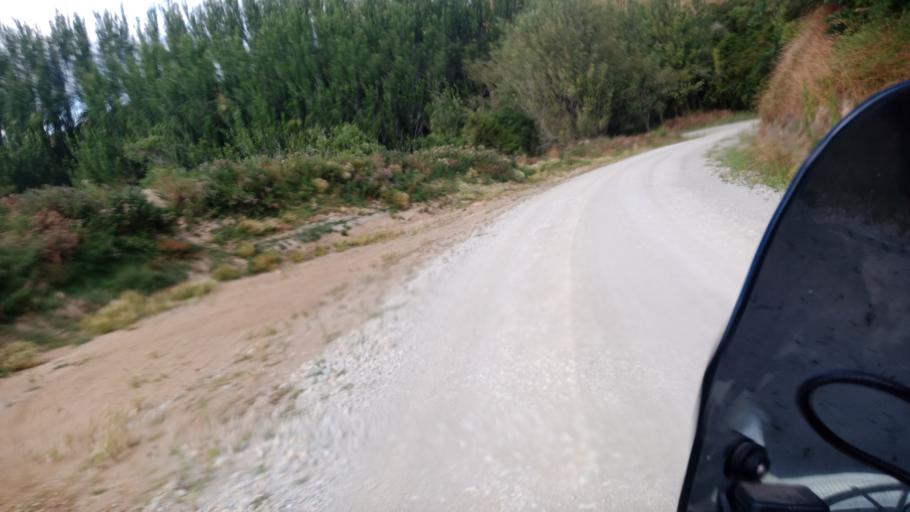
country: NZ
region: Hawke's Bay
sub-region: Wairoa District
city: Wairoa
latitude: -38.6056
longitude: 177.4652
